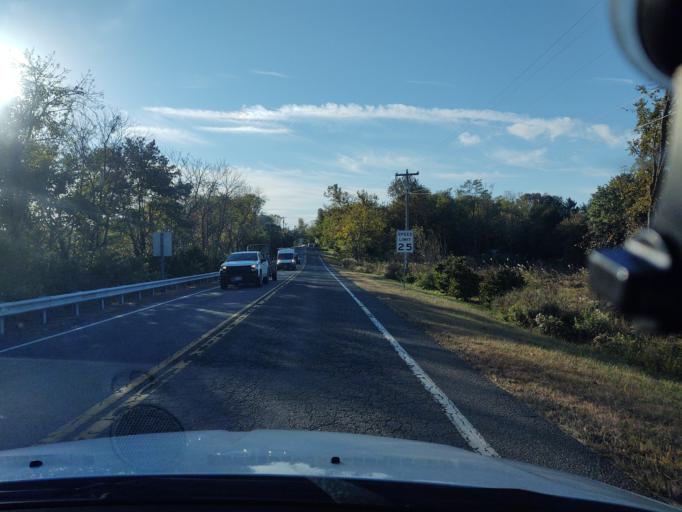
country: US
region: Maryland
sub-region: Queen Anne's County
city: Kingstown
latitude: 39.2437
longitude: -75.9241
